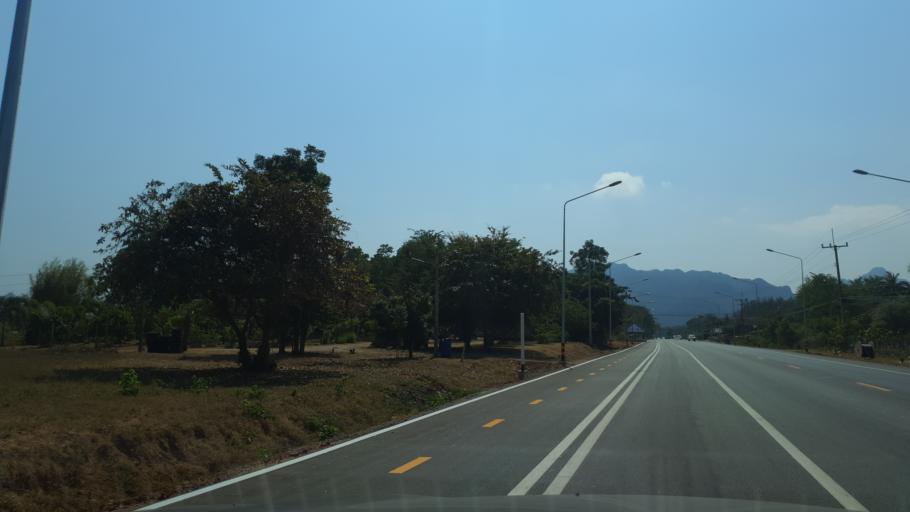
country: TH
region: Prachuap Khiri Khan
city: Sam Roi Yot
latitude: 12.2565
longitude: 99.9651
